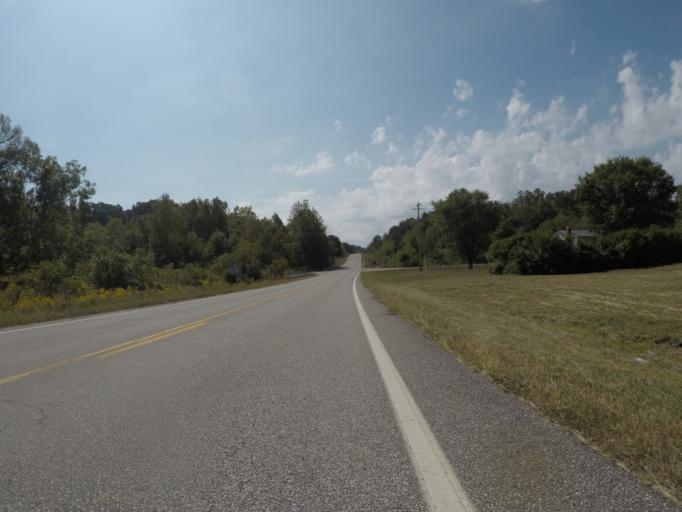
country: US
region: West Virginia
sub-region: Cabell County
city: Lesage
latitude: 38.5080
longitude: -82.3922
